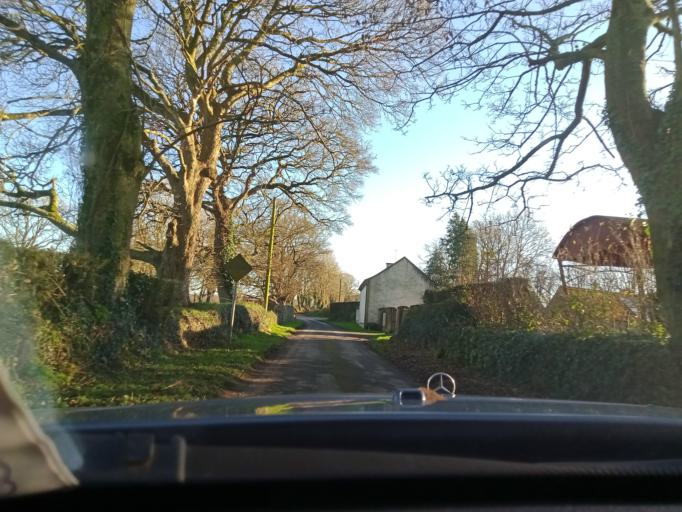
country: IE
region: Munster
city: Carrick-on-Suir
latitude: 52.4384
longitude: -7.3949
